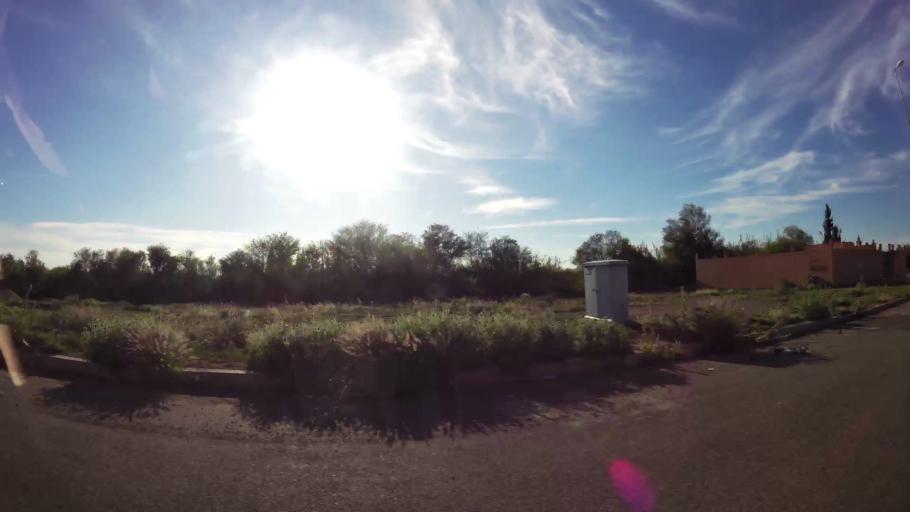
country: MA
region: Marrakech-Tensift-Al Haouz
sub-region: Marrakech
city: Marrakesh
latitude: 31.6790
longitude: -8.0682
